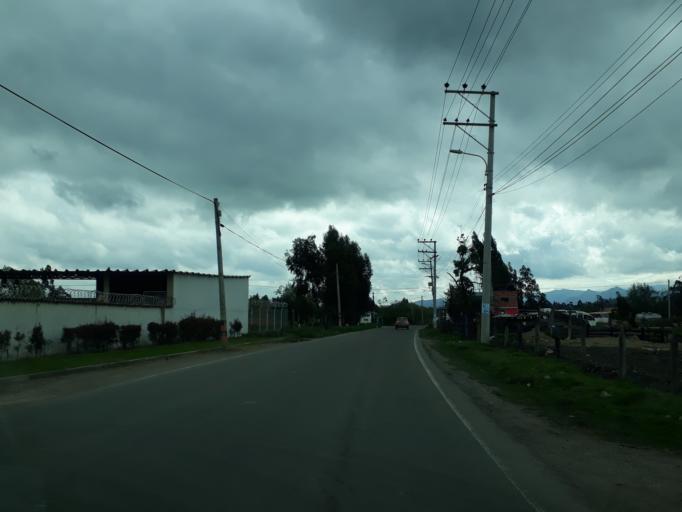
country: CO
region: Cundinamarca
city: Ubate
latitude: 5.3167
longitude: -73.8010
